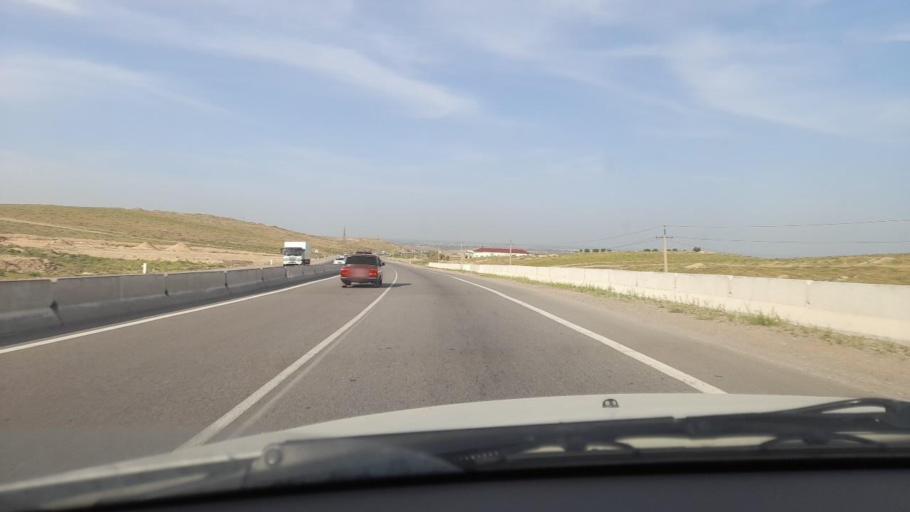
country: UZ
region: Jizzax
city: Jizzax
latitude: 40.0559
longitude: 67.8163
